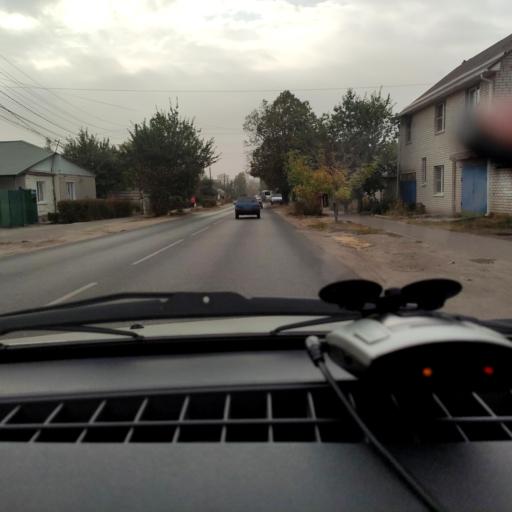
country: RU
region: Voronezj
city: Voronezh
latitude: 51.6982
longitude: 39.1895
